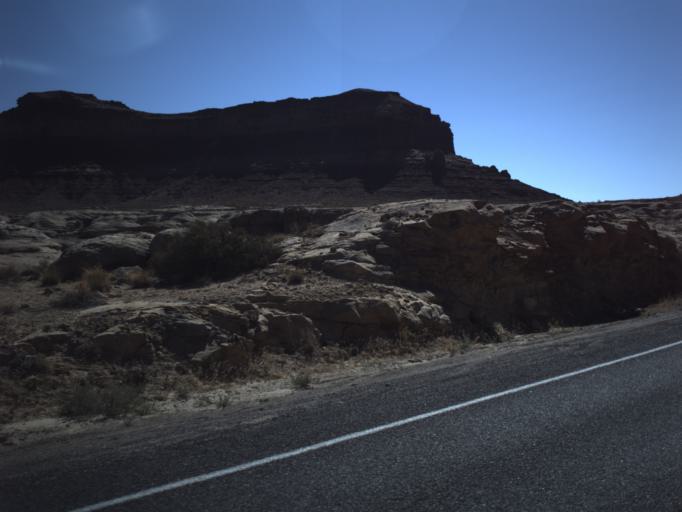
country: US
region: Utah
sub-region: San Juan County
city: Blanding
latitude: 37.9175
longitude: -110.3882
